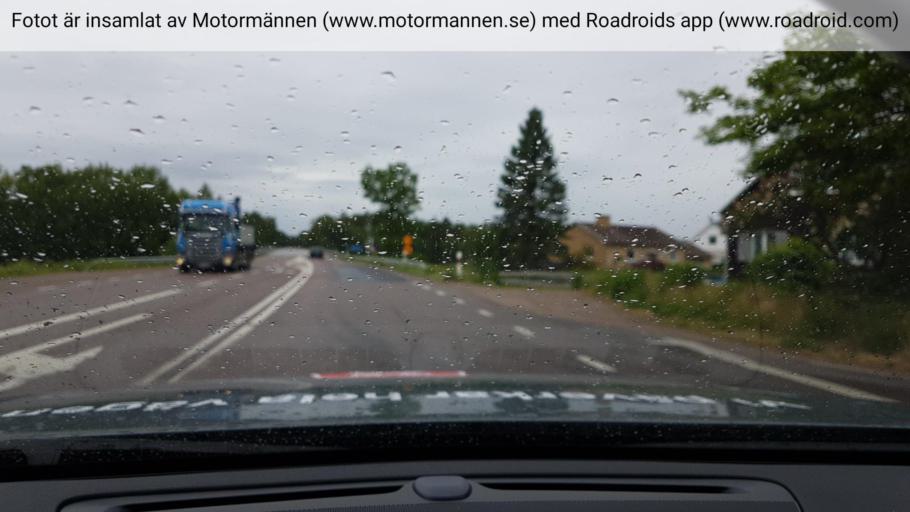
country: SE
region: Uppsala
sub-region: Alvkarleby Kommun
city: AElvkarleby
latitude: 60.6018
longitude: 17.4543
